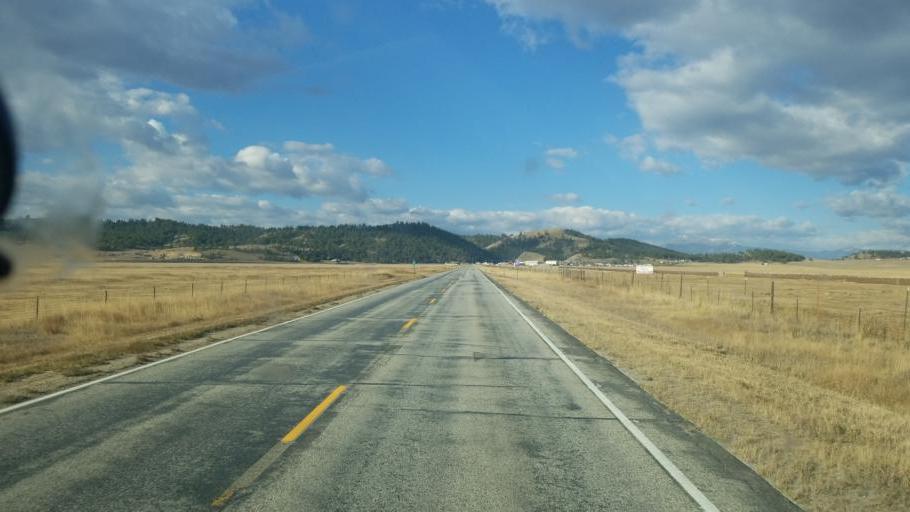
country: US
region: Colorado
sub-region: Park County
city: Fairplay
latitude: 39.0263
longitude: -105.7805
